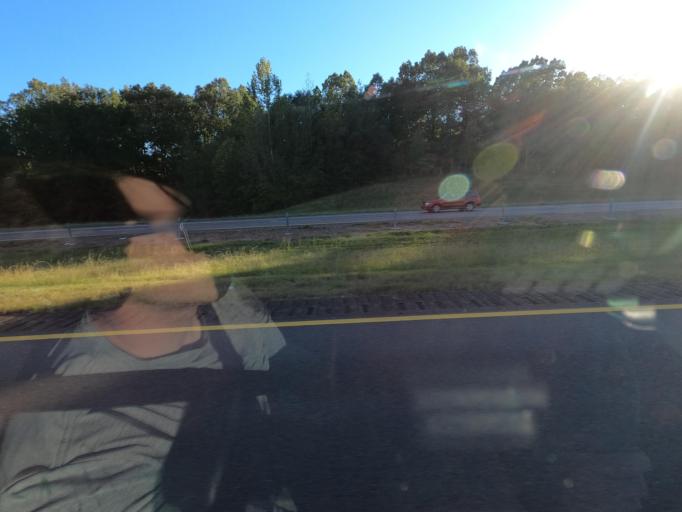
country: US
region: Tennessee
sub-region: Shelby County
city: Arlington
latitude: 35.3106
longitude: -89.7100
